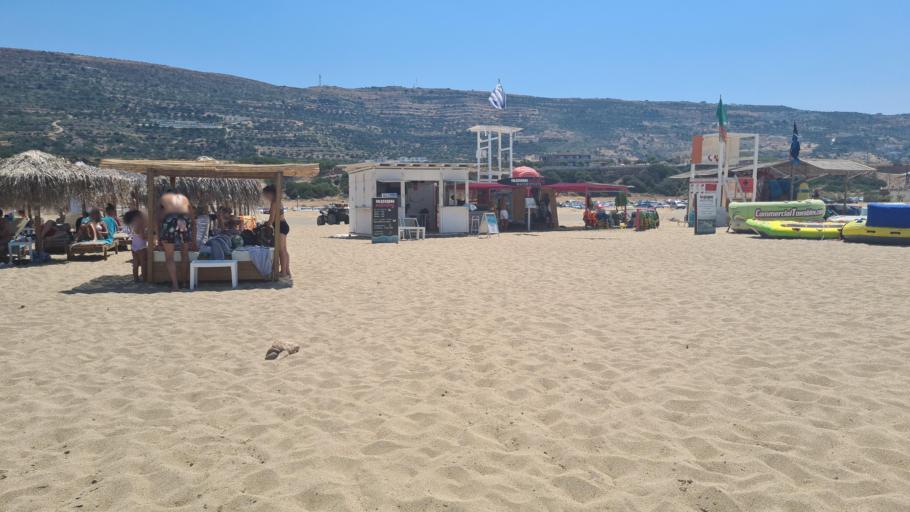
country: GR
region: Crete
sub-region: Nomos Chanias
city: Platanos
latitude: 35.4918
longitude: 23.5795
